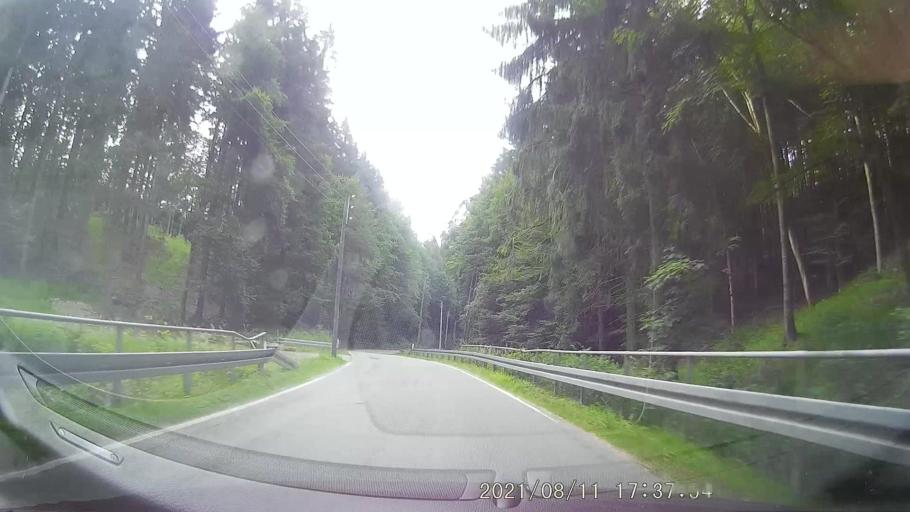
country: PL
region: Lower Silesian Voivodeship
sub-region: Powiat klodzki
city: Duszniki-Zdroj
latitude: 50.3408
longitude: 16.4023
